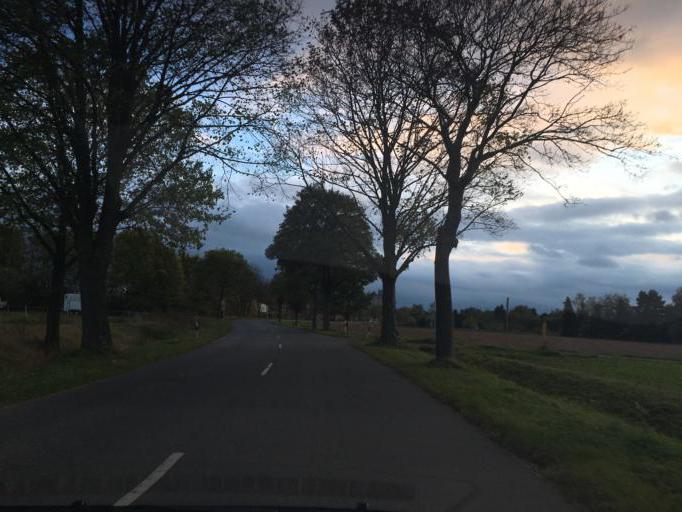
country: DE
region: North Rhine-Westphalia
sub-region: Regierungsbezirk Koln
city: Vettweiss
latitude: 50.7466
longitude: 6.6063
